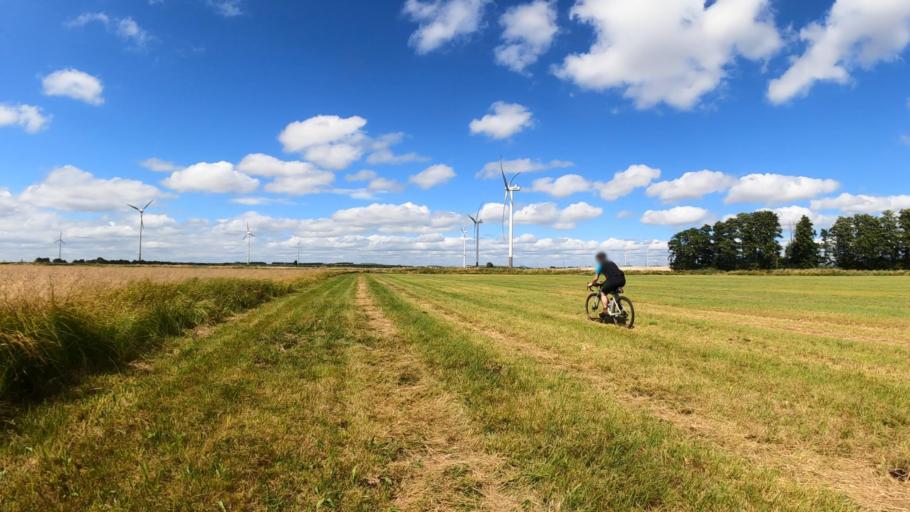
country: DE
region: Lower Saxony
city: Neu Wulmstorf
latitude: 53.4932
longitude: 9.8527
